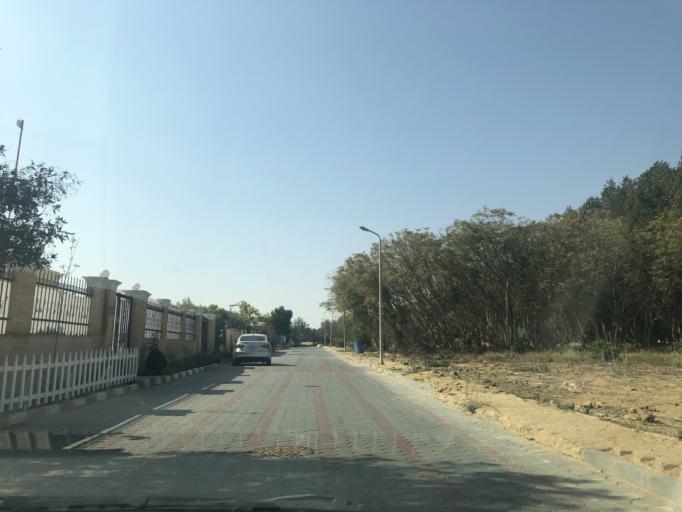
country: EG
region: Al Jizah
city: Madinat Sittah Uktubar
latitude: 29.9571
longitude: 31.0086
